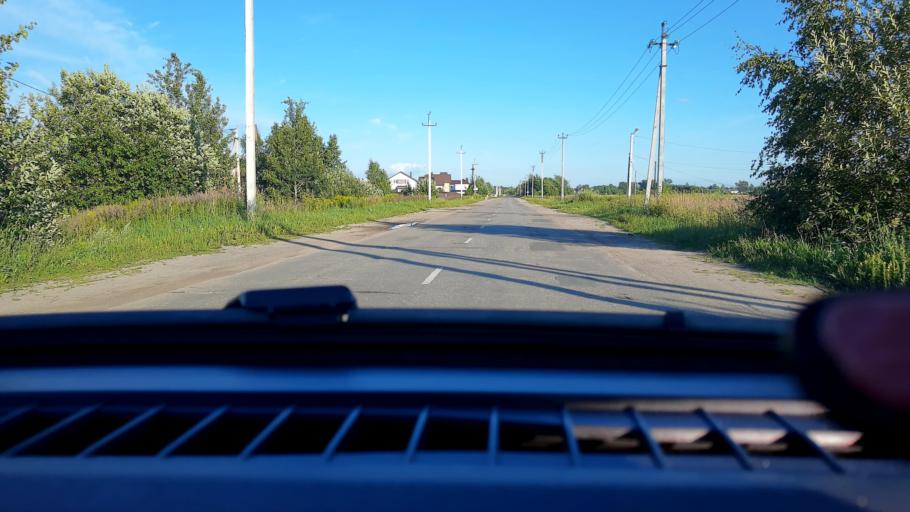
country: RU
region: Nizjnij Novgorod
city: Bor
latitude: 56.3500
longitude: 44.1308
